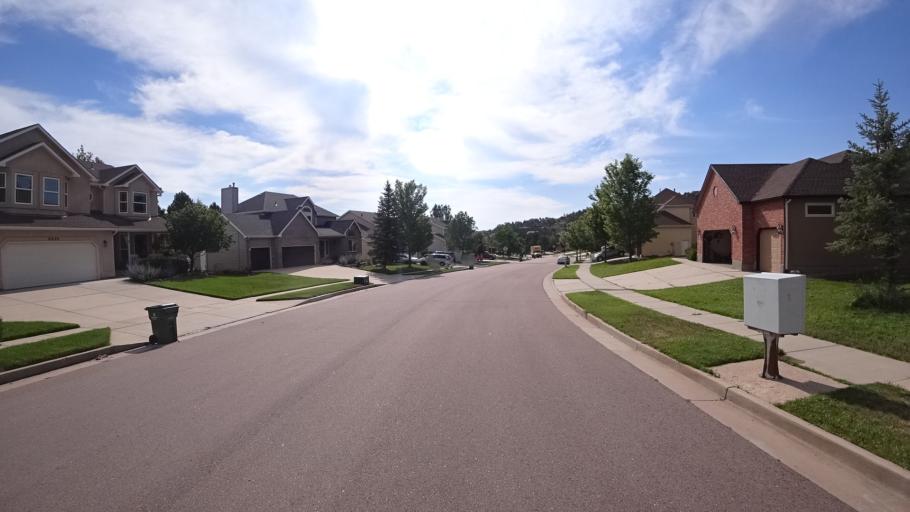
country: US
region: Colorado
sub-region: El Paso County
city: Air Force Academy
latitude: 38.9436
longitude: -104.8688
